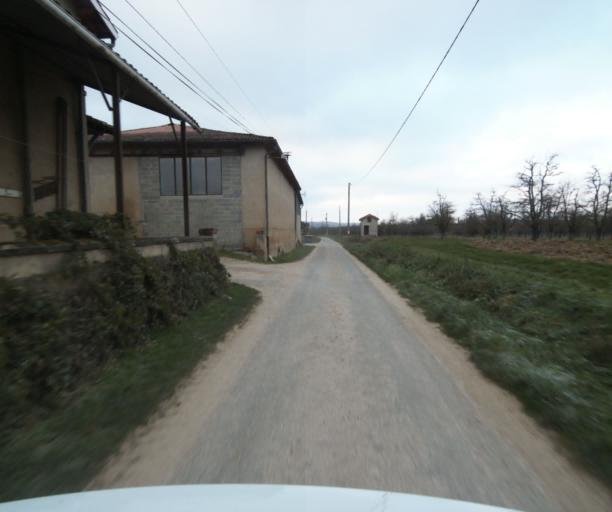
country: FR
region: Midi-Pyrenees
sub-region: Departement du Tarn-et-Garonne
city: Moissac
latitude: 44.0980
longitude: 1.1245
